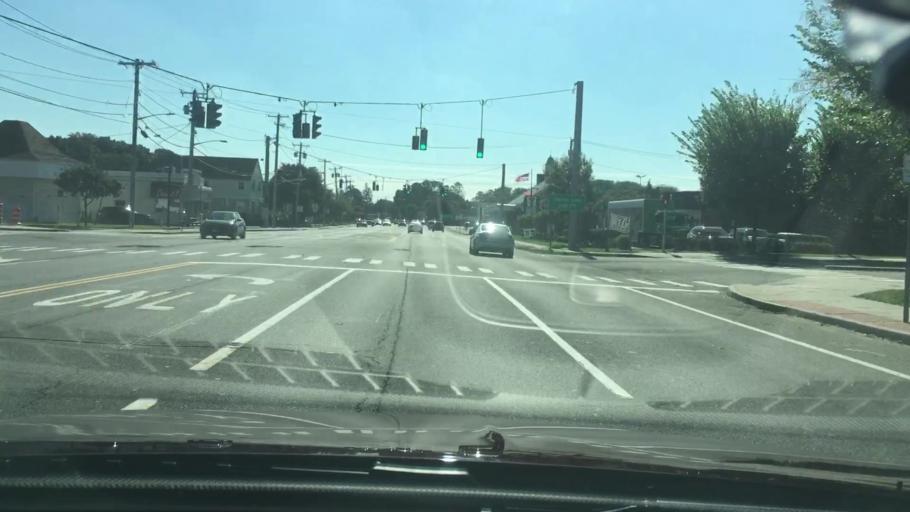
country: US
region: New York
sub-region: Suffolk County
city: Port Jefferson Station
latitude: 40.9321
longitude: -73.0531
